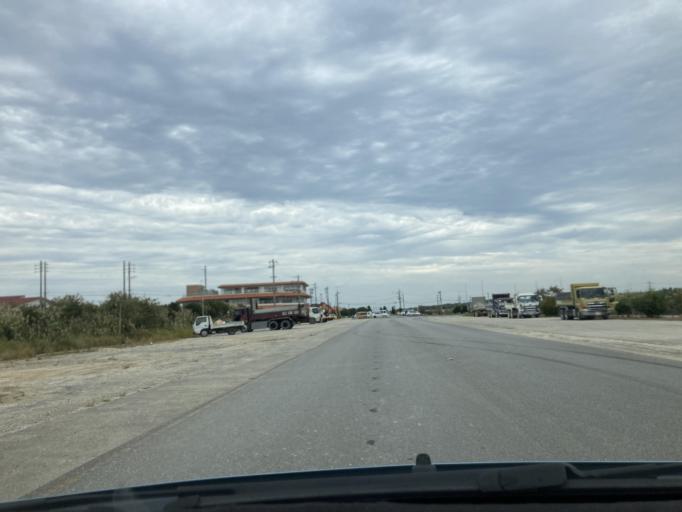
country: JP
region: Okinawa
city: Okinawa
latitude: 26.3914
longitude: 127.7465
